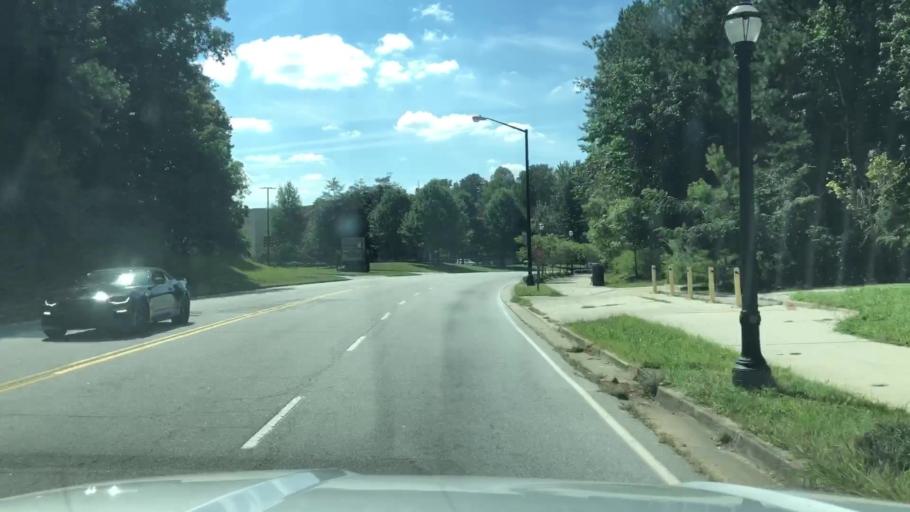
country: US
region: Georgia
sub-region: Fulton County
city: College Park
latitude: 33.6850
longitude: -84.4979
